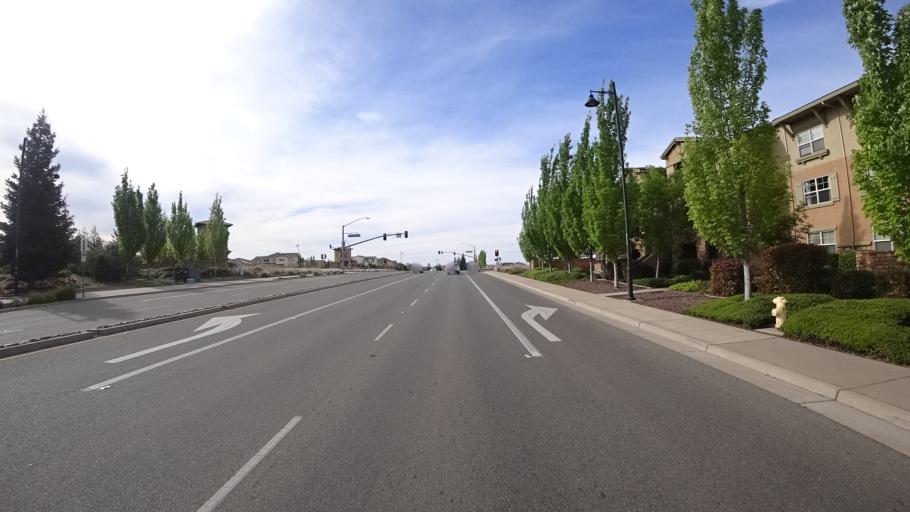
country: US
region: California
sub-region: Placer County
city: Lincoln
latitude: 38.8313
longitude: -121.2885
